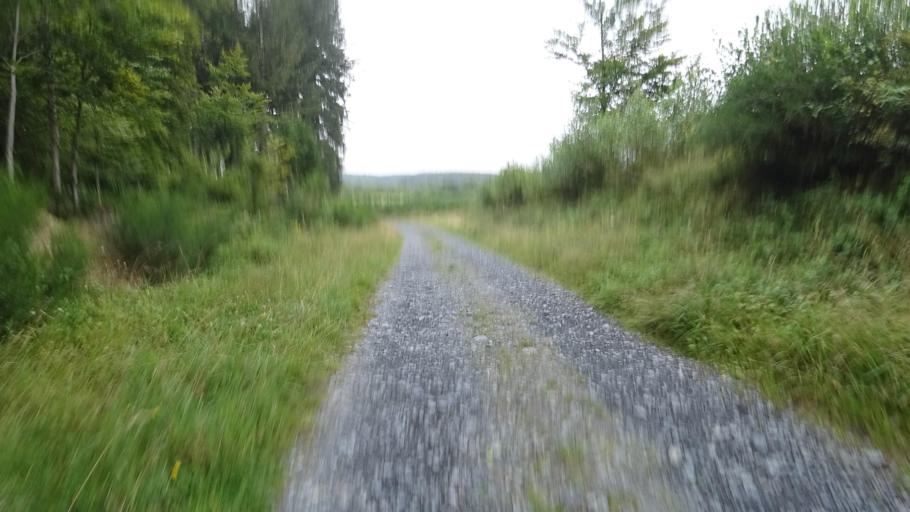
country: BE
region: Wallonia
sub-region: Province du Luxembourg
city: Chiny
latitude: 49.7886
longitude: 5.3237
